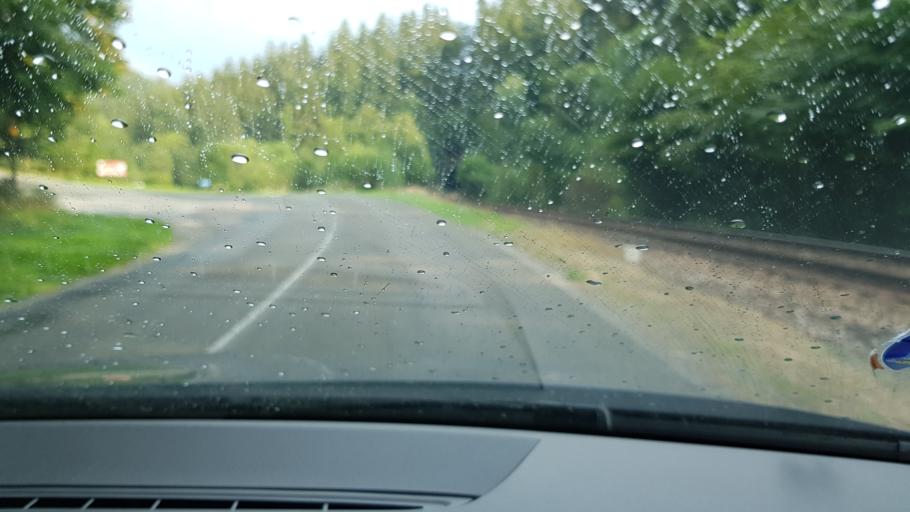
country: CZ
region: Olomoucky
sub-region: Okres Sumperk
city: Hanusovice
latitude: 50.0923
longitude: 16.8725
